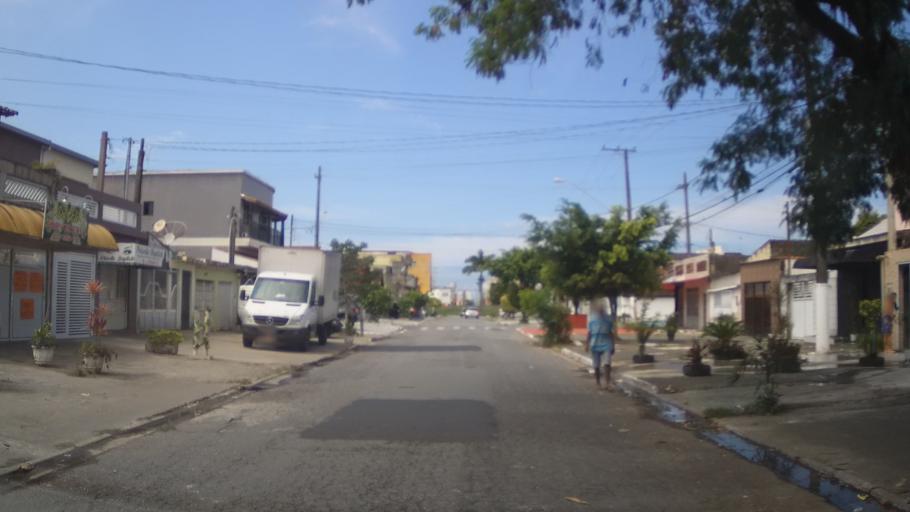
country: BR
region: Sao Paulo
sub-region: Praia Grande
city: Praia Grande
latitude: -24.0204
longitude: -46.4829
